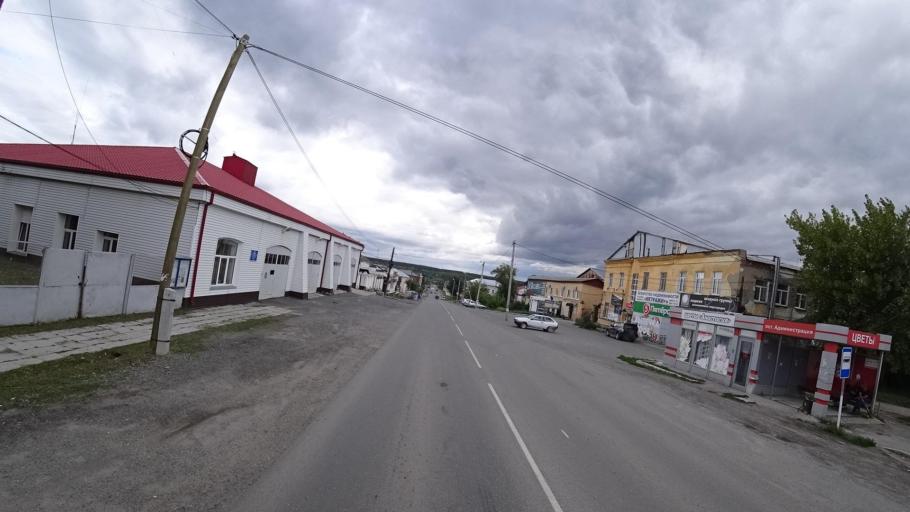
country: RU
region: Sverdlovsk
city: Kamyshlov
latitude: 56.8474
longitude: 62.6993
